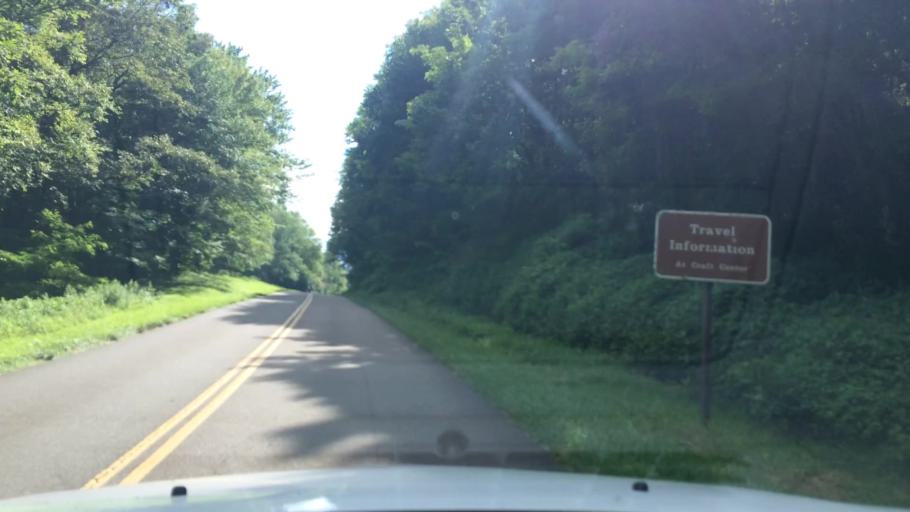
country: US
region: North Carolina
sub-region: Watauga County
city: Blowing Rock
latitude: 36.1521
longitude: -81.6877
